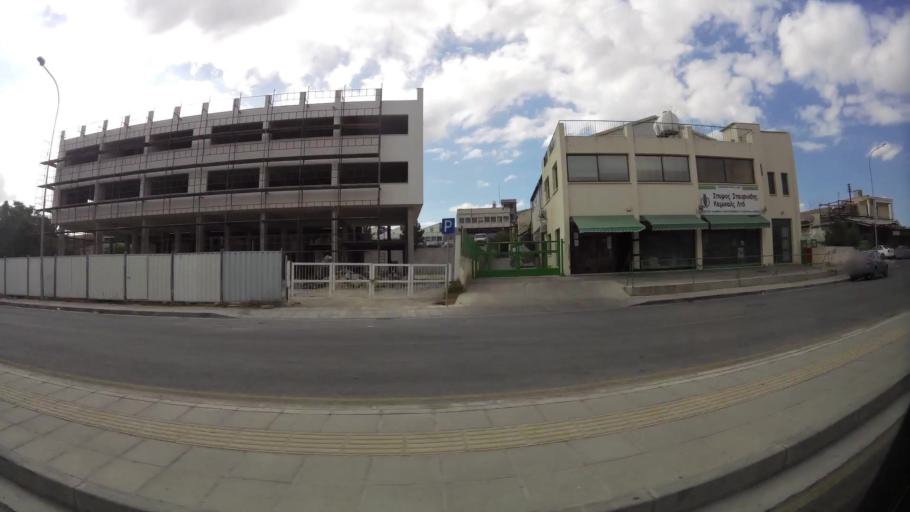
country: CY
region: Lefkosia
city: Nicosia
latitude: 35.1813
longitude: 33.3946
